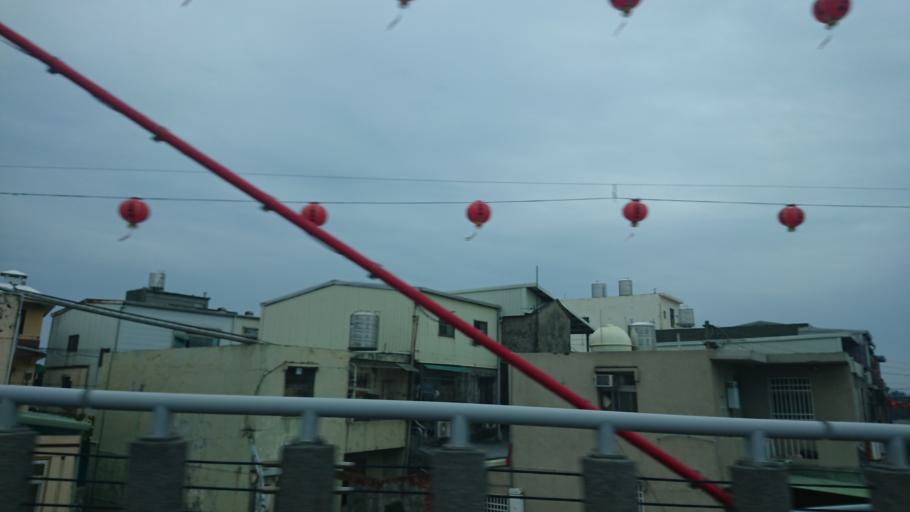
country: TW
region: Taiwan
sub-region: Hsinchu
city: Hsinchu
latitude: 24.8441
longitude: 120.9429
